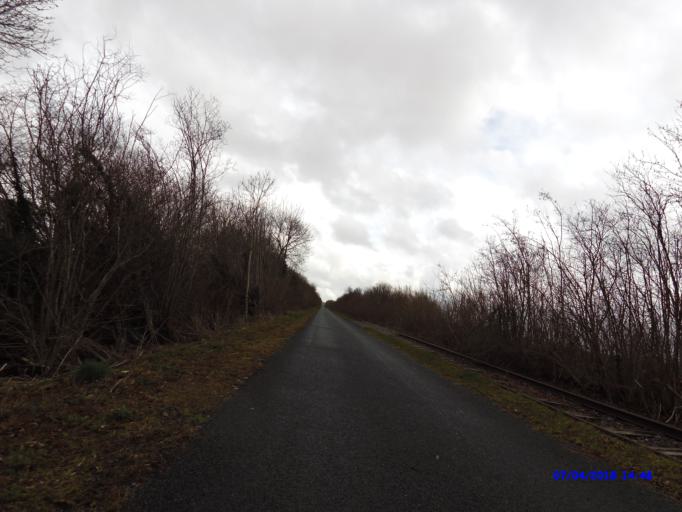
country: IE
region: Leinster
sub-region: An Iarmhi
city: Athlone
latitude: 53.4169
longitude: -7.8688
